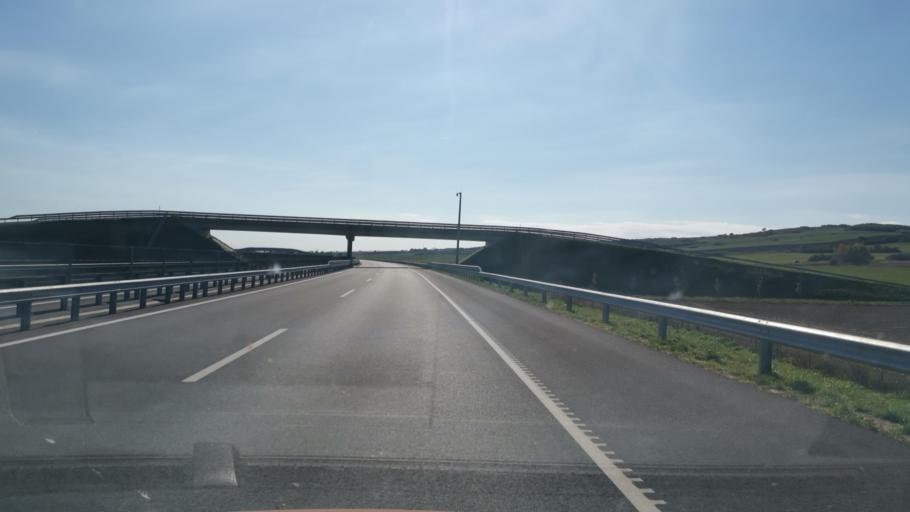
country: HU
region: Borsod-Abauj-Zemplen
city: Szikszo
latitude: 48.1963
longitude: 20.9067
